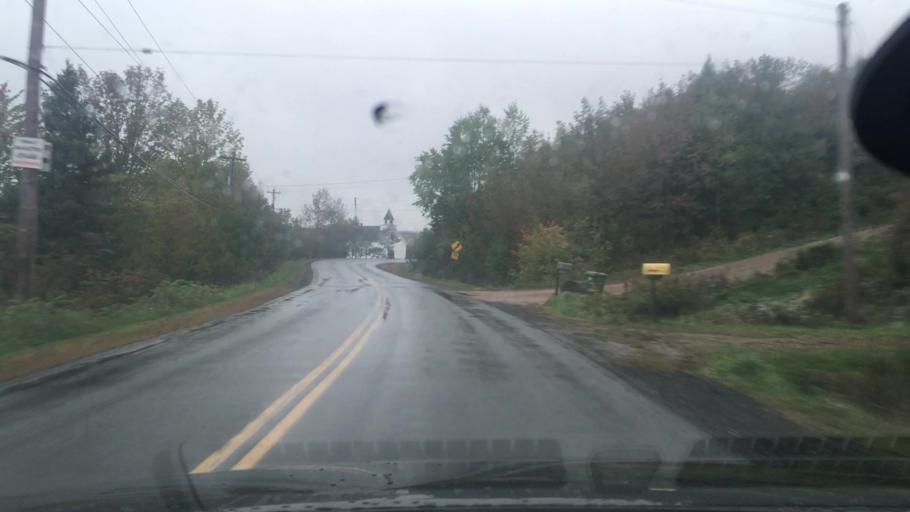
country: CA
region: Nova Scotia
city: Windsor
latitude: 44.8405
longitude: -64.2340
